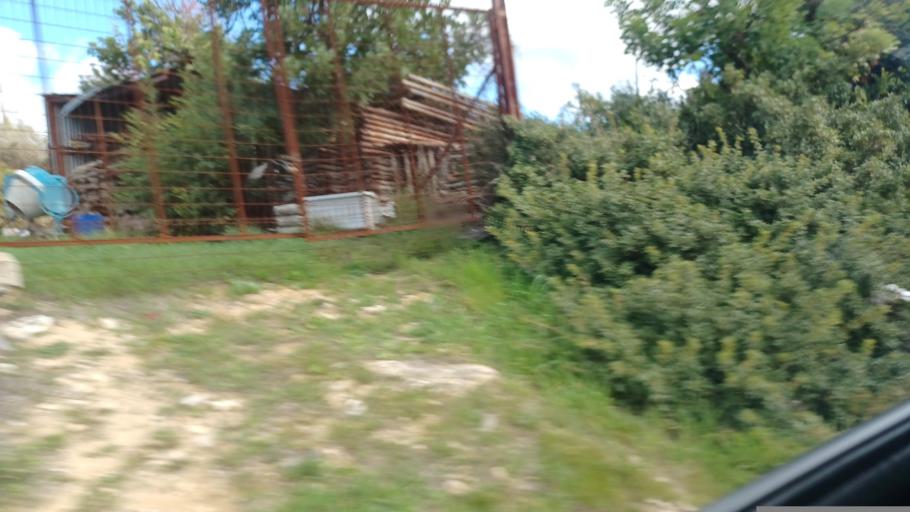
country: CY
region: Limassol
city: Pano Polemidia
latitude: 34.7834
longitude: 32.9800
